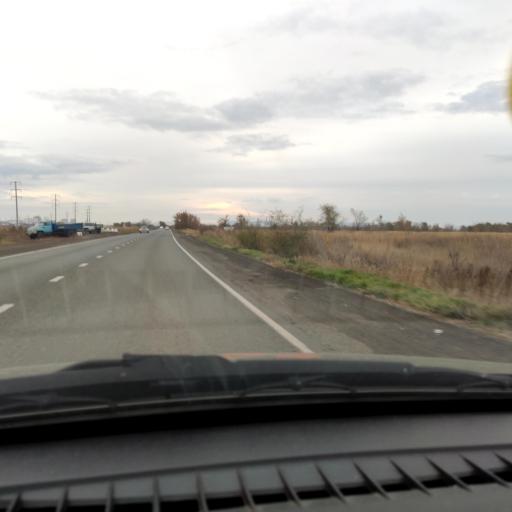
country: RU
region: Samara
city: Podstepki
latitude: 53.5217
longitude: 49.2009
